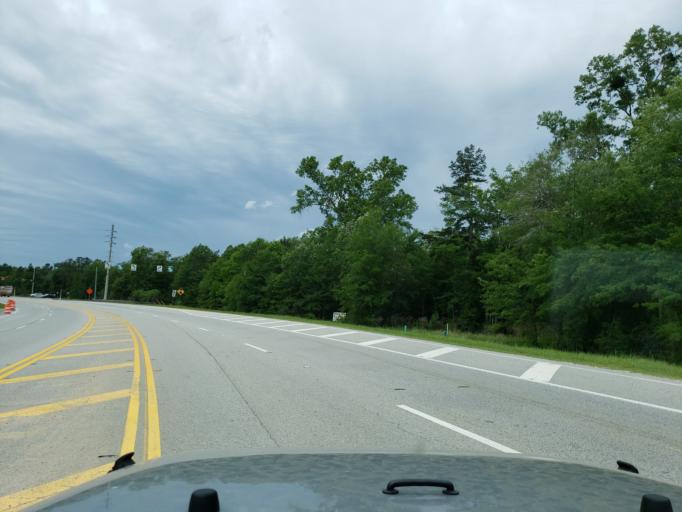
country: US
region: Georgia
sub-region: Effingham County
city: Rincon
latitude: 32.2402
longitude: -81.1956
